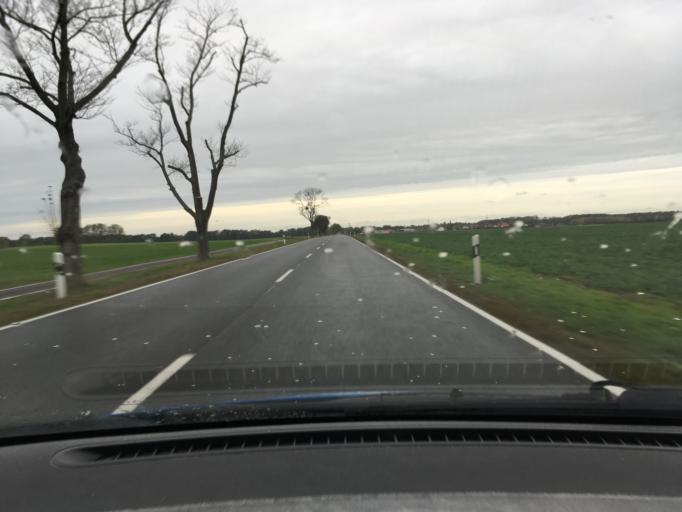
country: DE
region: Saxony-Anhalt
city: Rodleben
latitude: 51.9282
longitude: 12.1491
